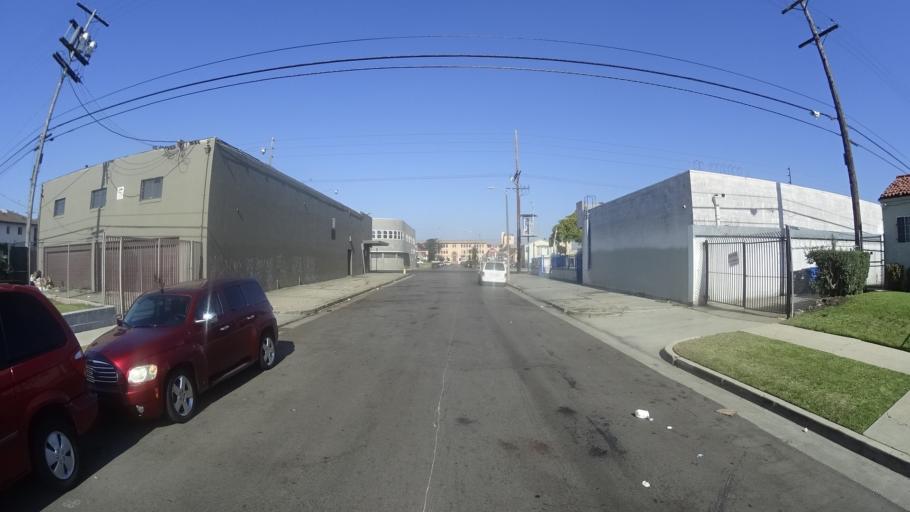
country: US
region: California
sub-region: Los Angeles County
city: Westmont
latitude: 33.9762
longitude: -118.3083
